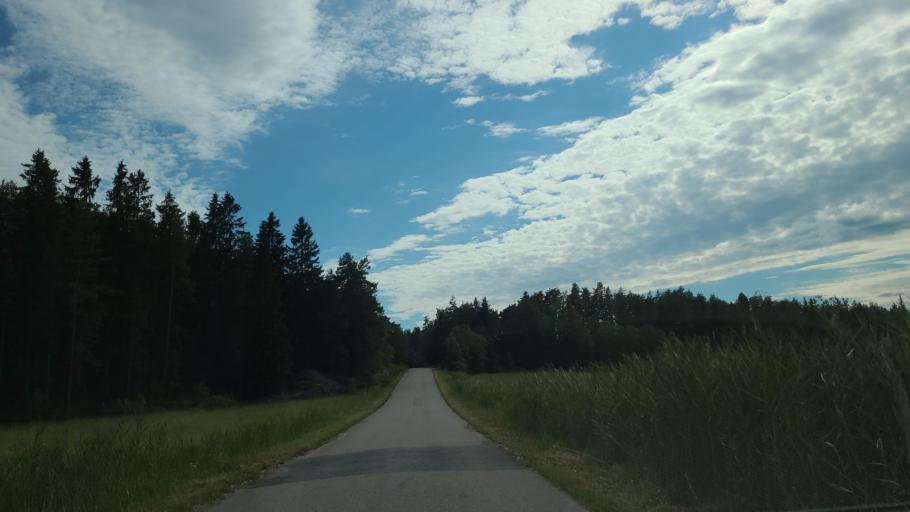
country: FI
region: Varsinais-Suomi
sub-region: Turku
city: Rymaettylae
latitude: 60.3097
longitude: 21.9438
